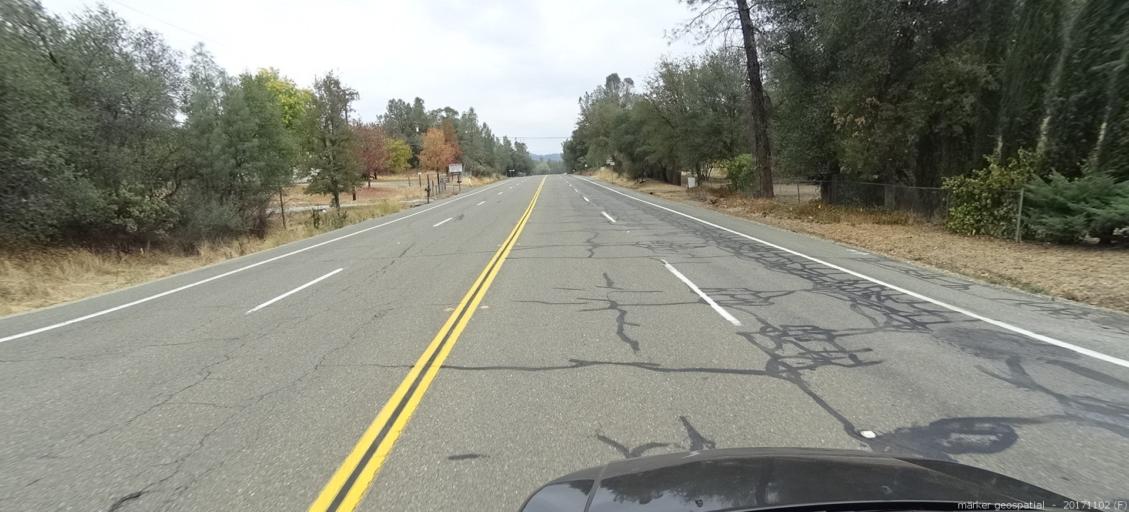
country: US
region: California
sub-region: Shasta County
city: Central Valley (historical)
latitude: 40.6506
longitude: -122.3971
